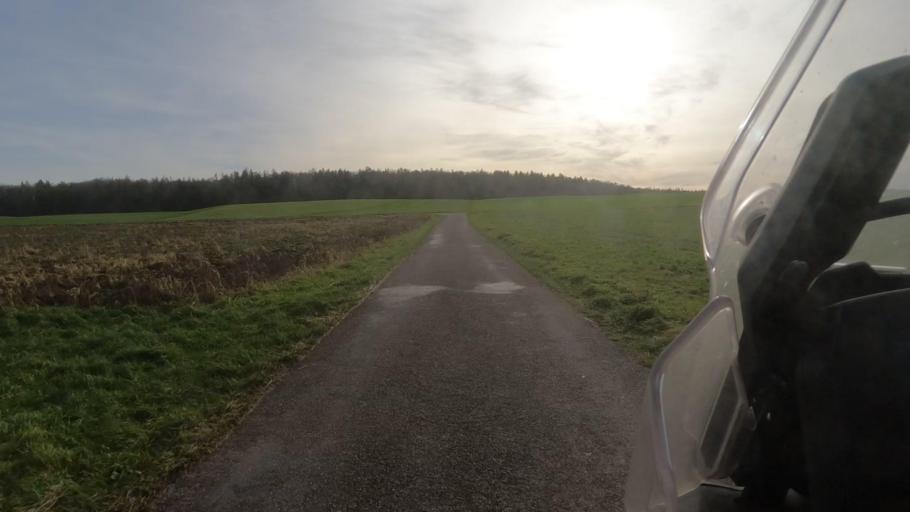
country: CH
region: Zurich
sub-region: Bezirk Buelach
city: Glattfelden
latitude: 47.5441
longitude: 8.5045
